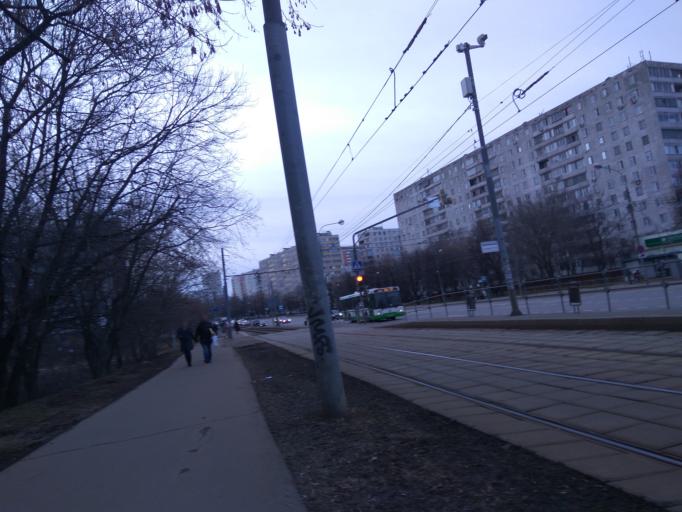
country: RU
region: Moscow
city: Leonovo
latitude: 55.8713
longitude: 37.6526
